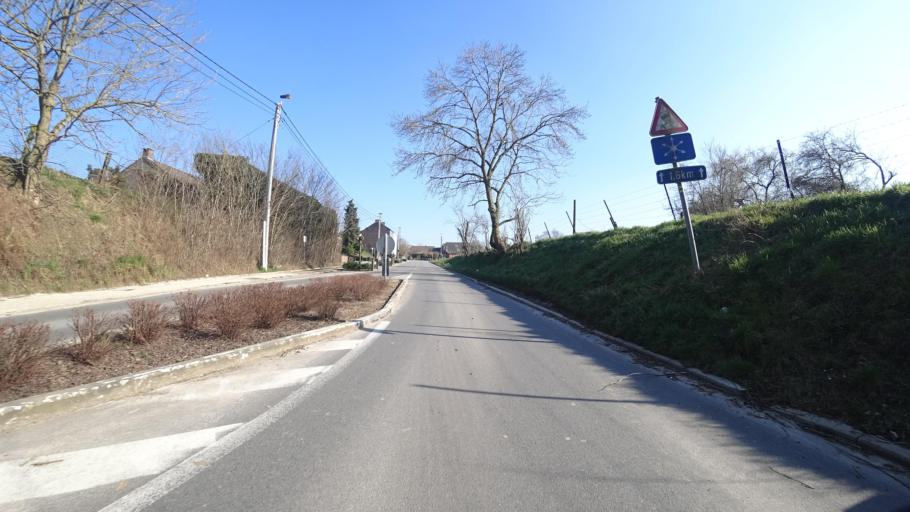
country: BE
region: Wallonia
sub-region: Province du Brabant Wallon
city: Chastre
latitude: 50.6019
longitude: 4.6099
